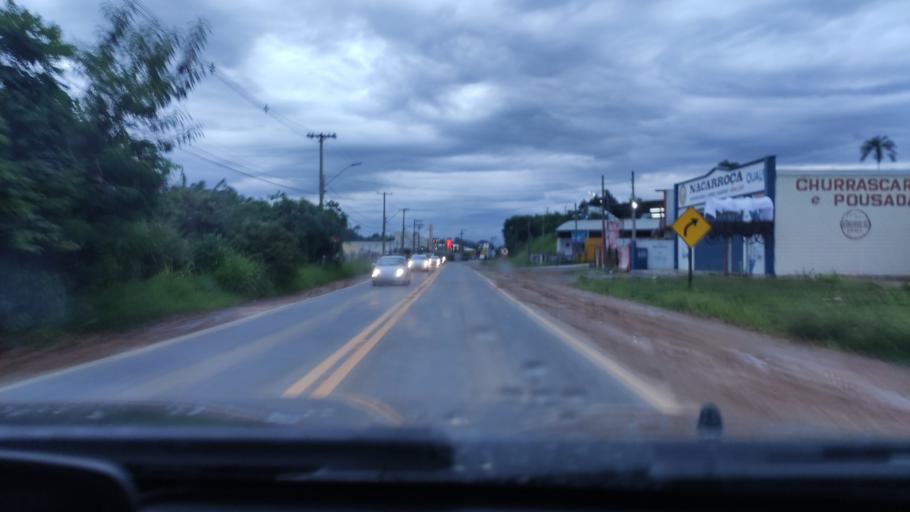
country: BR
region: Sao Paulo
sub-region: Socorro
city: Socorro
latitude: -22.6224
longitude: -46.5342
